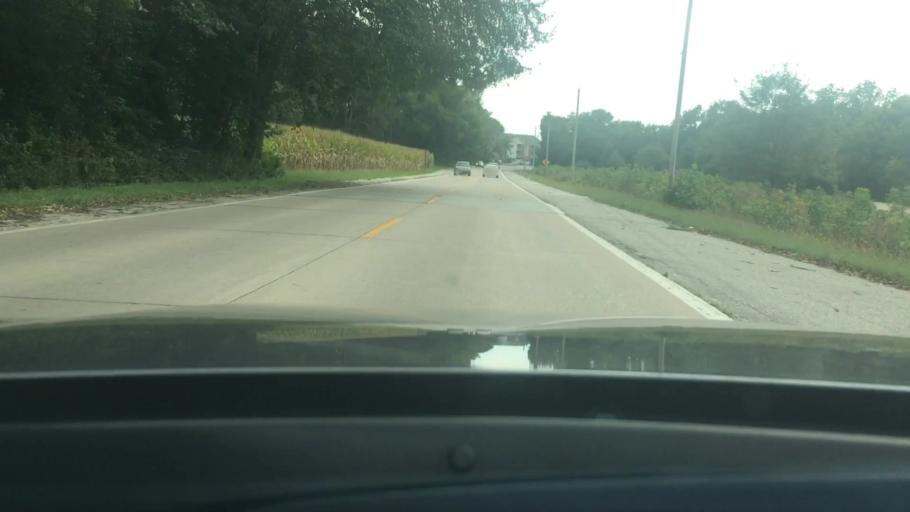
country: US
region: Iowa
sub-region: Pottawattamie County
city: Council Bluffs
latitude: 41.2562
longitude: -95.8089
